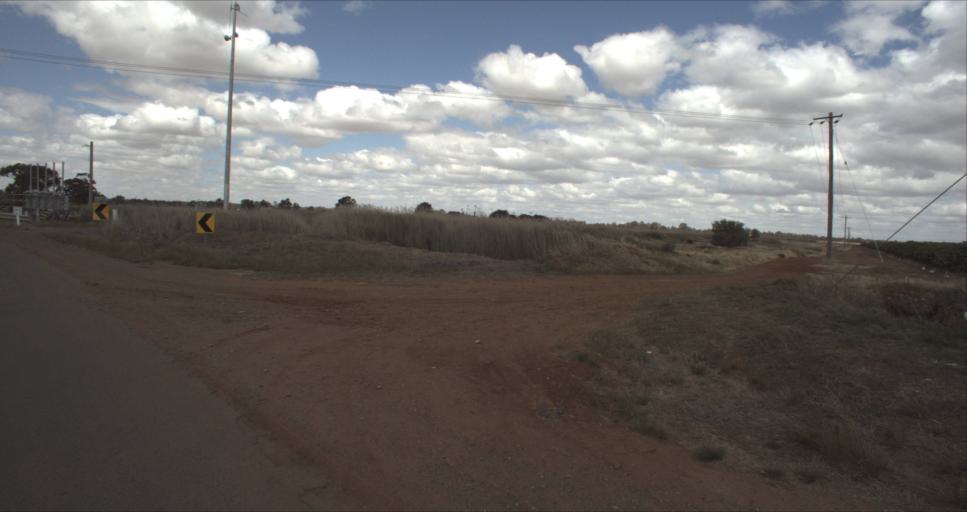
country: AU
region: New South Wales
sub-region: Leeton
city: Leeton
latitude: -34.5887
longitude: 146.3851
